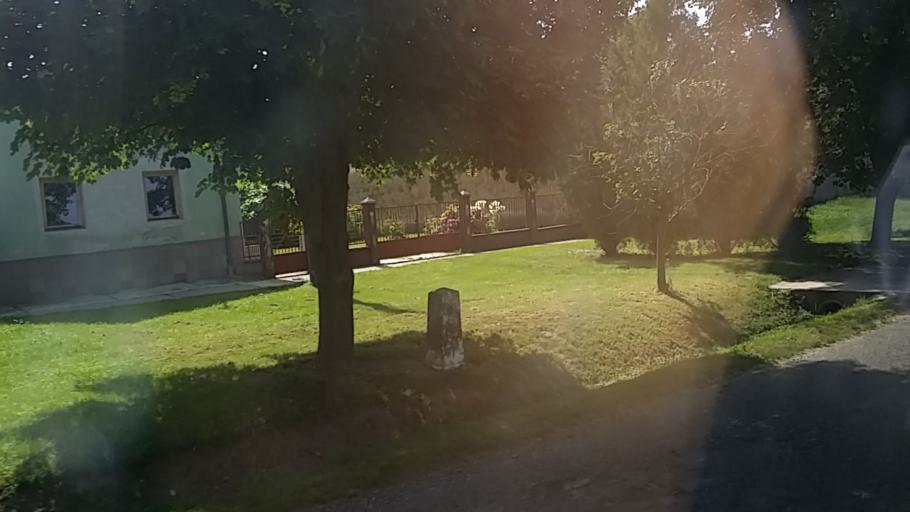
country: HU
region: Baranya
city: Siklos
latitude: 45.9109
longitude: 18.3364
